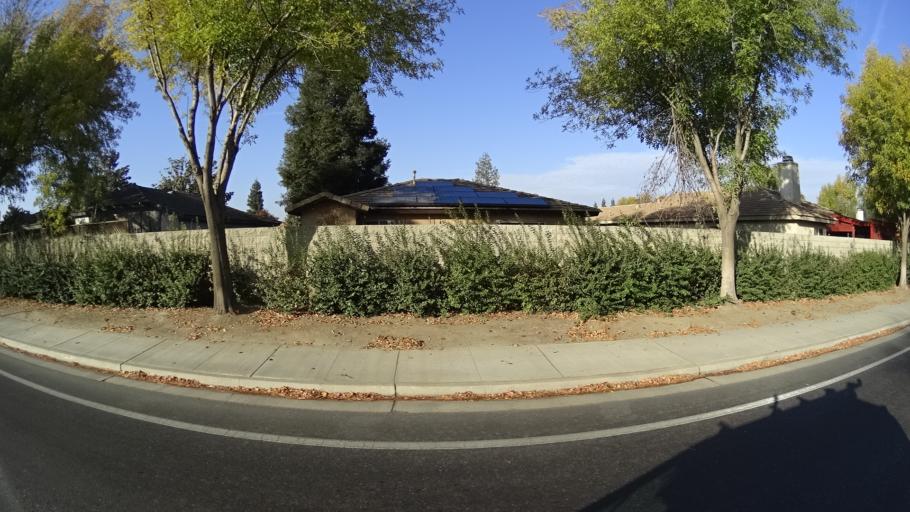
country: US
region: California
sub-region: Kern County
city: Greenacres
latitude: 35.3246
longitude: -119.0923
